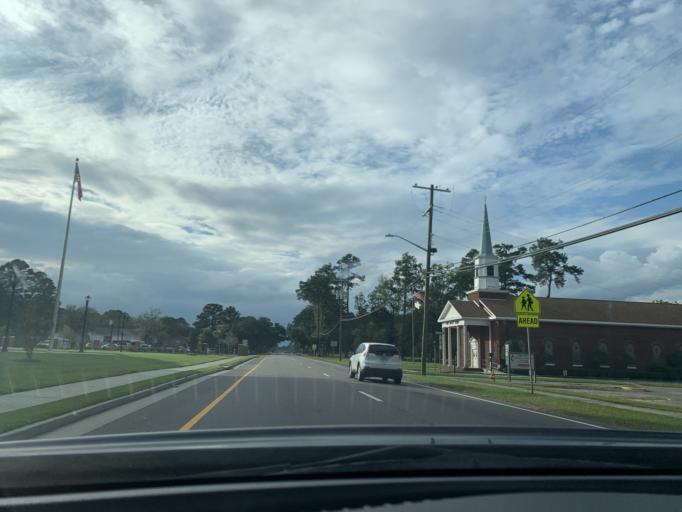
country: US
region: Georgia
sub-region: Chatham County
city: Pooler
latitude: 32.1163
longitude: -81.2495
